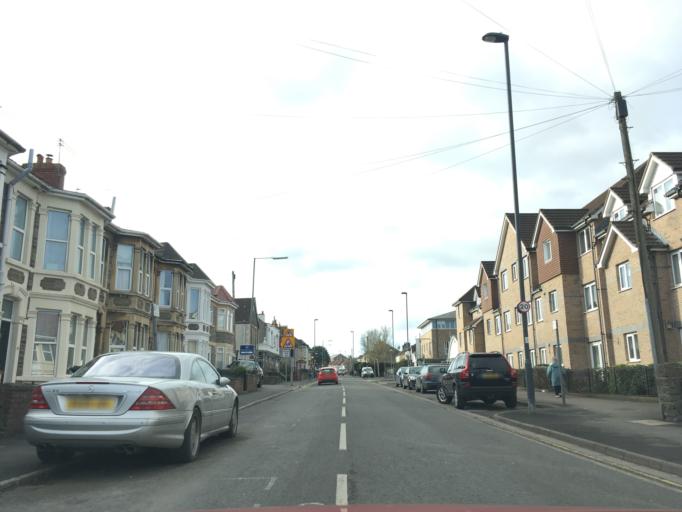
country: GB
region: England
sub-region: South Gloucestershire
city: Mangotsfield
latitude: 51.4862
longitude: -2.5049
